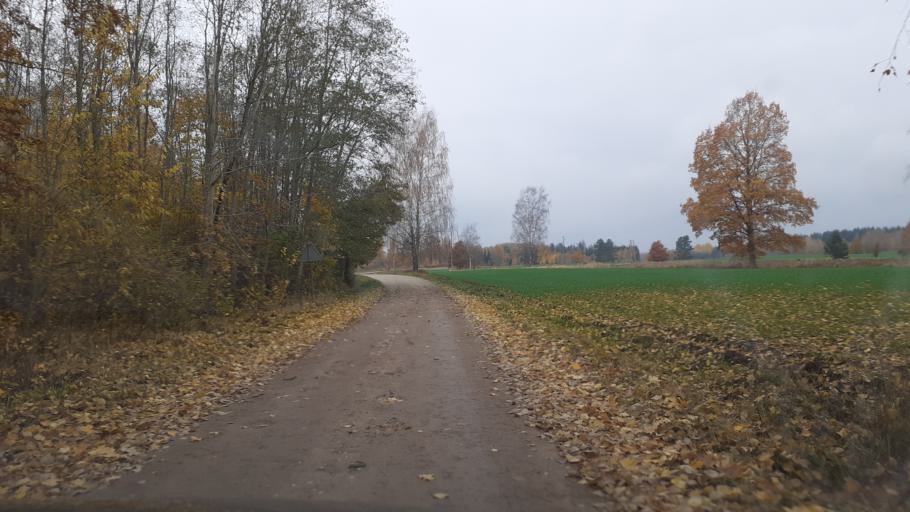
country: LV
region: Saldus Rajons
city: Saldus
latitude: 56.8774
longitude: 22.2953
